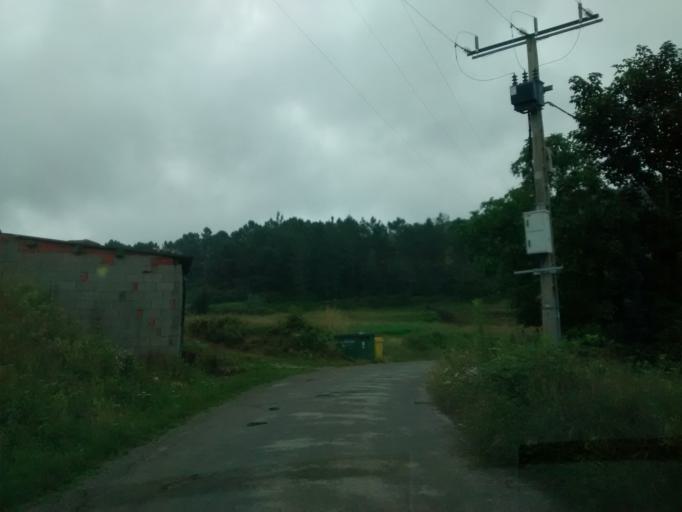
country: ES
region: Galicia
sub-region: Provincia de Ourense
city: Castro Caldelas
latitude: 42.4053
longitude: -7.3986
